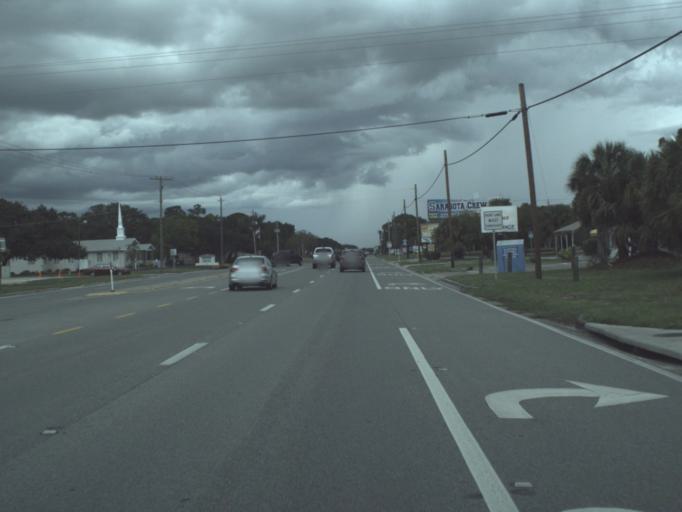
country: US
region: Florida
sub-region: Sarasota County
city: Osprey
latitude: 27.1990
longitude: -82.4902
